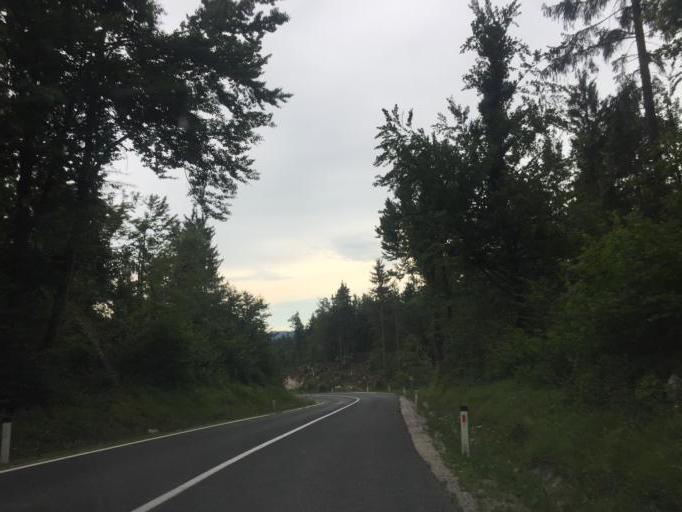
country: SI
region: Logatec
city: Logatec
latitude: 45.9112
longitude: 14.1591
